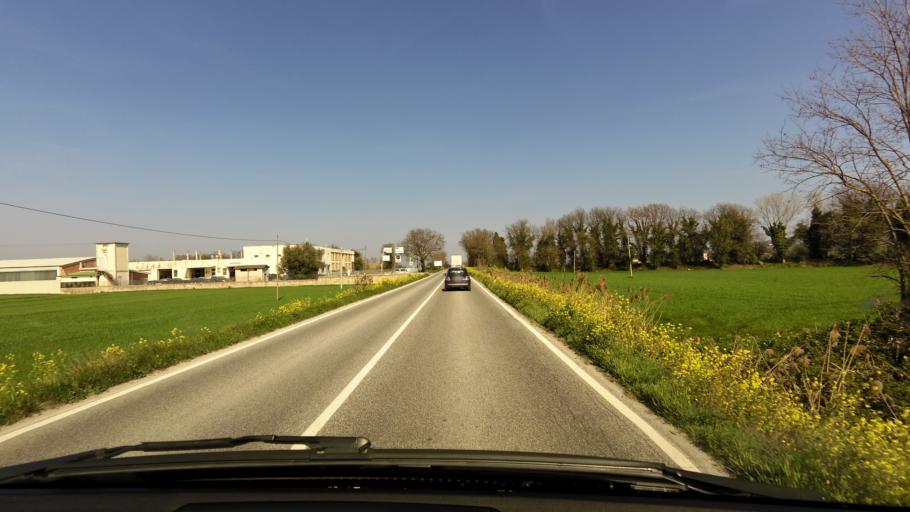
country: IT
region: The Marches
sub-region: Provincia di Macerata
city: Potenza Picena
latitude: 43.3814
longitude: 13.6115
